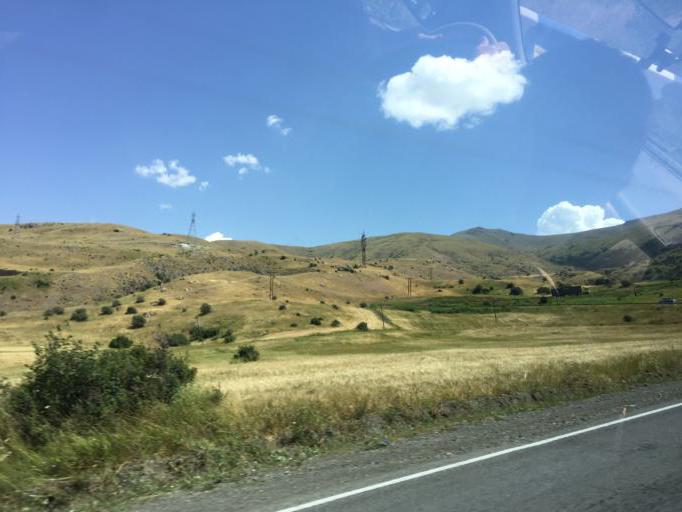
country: AM
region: Vayots' Dzori Marz
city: Jermuk
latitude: 39.7120
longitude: 45.6614
